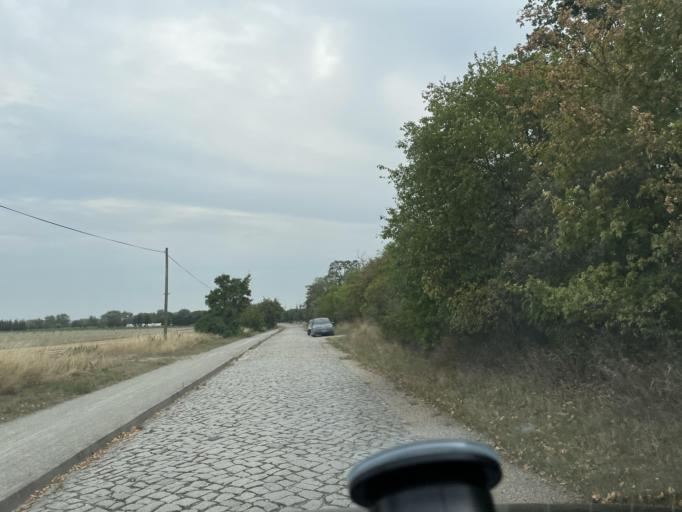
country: DE
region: Saxony-Anhalt
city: Calbe
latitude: 51.9083
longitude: 11.7487
